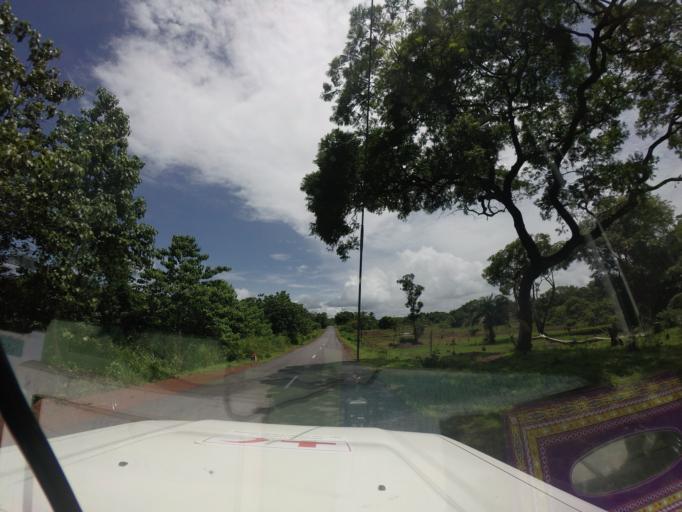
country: GN
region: Faranah
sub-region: Faranah Prefecture
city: Faranah
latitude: 10.0154
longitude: -10.8786
